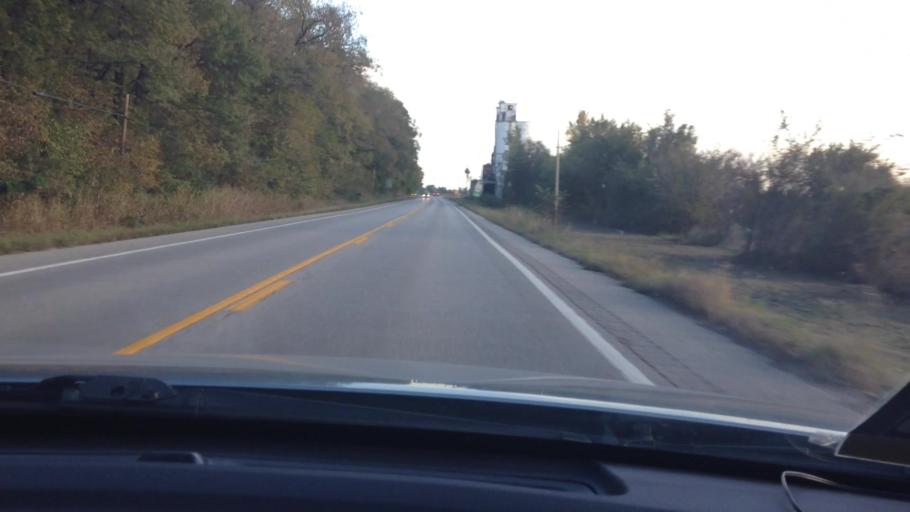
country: US
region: Kansas
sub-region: Leavenworth County
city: Lansing
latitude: 39.2835
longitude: -94.8365
